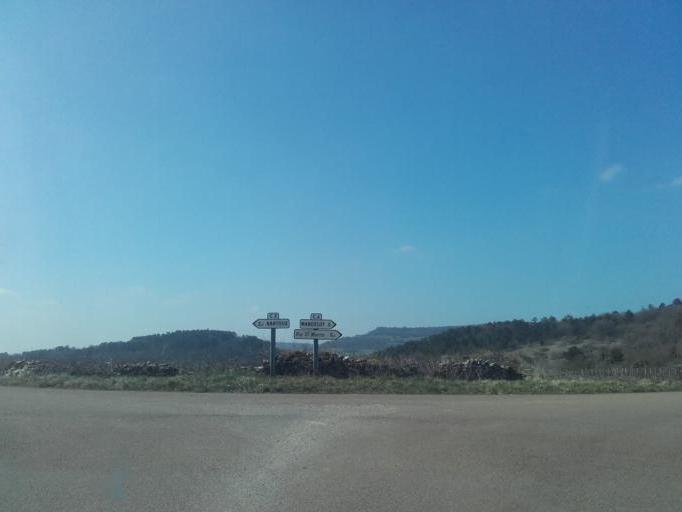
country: FR
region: Bourgogne
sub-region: Departement de la Cote-d'Or
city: Savigny-les-Beaune
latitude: 47.0534
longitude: 4.7619
